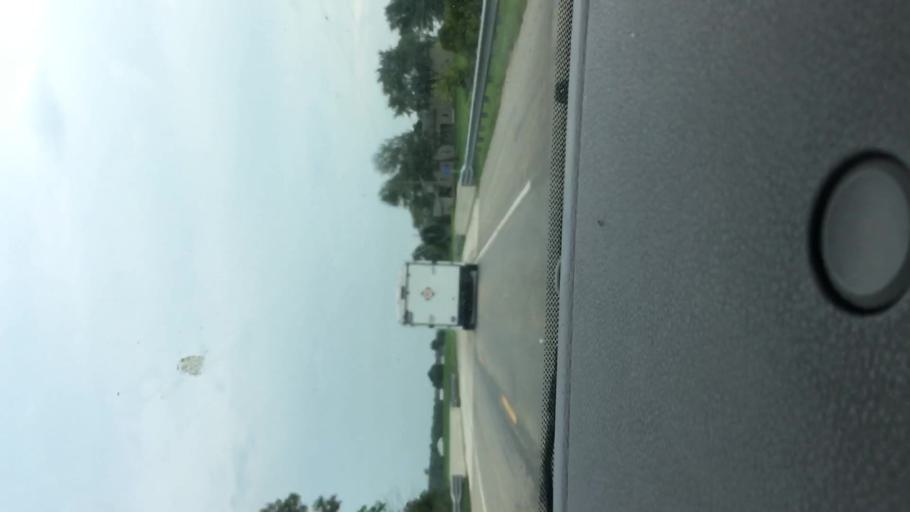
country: US
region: Indiana
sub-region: Adams County
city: Geneva
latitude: 40.5414
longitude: -84.9435
